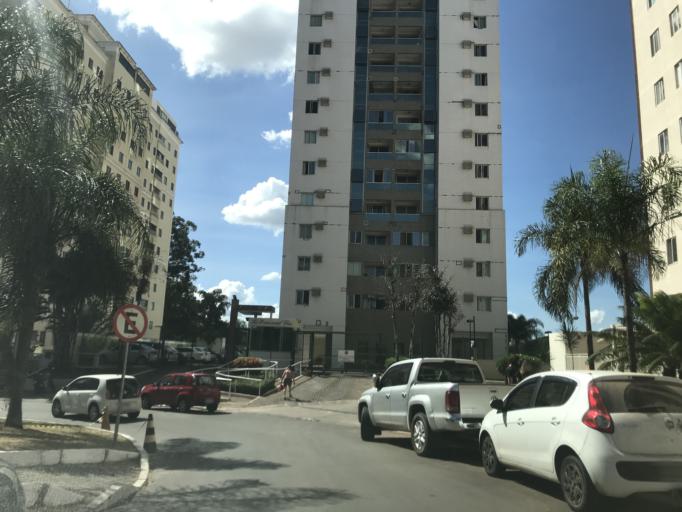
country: BR
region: Federal District
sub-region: Brasilia
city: Brasilia
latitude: -15.8325
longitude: -48.0103
